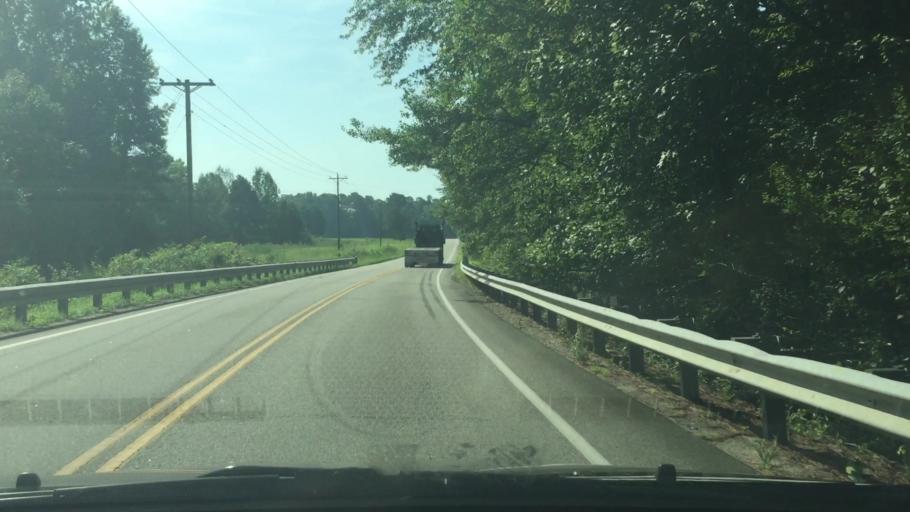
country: US
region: Virginia
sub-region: Sussex County
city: Sussex
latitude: 37.0476
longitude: -77.3146
